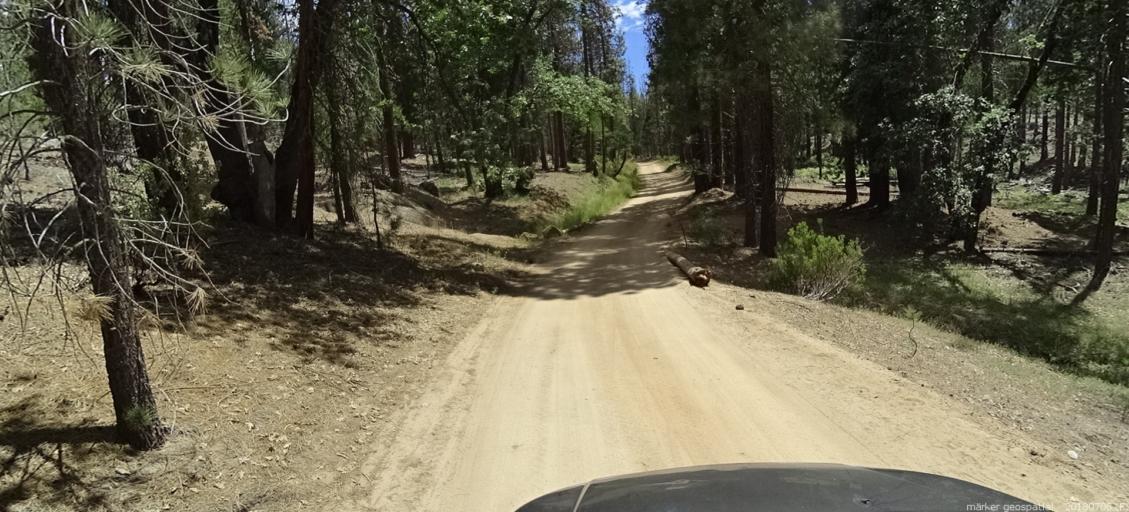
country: US
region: California
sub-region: Madera County
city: Oakhurst
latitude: 37.4162
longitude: -119.3793
